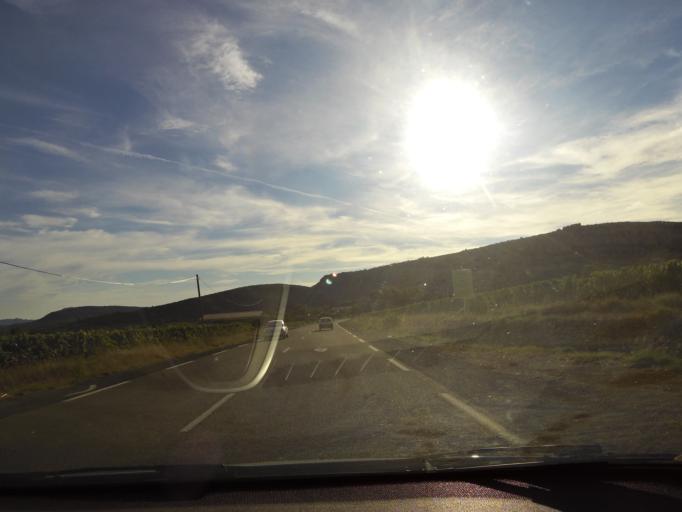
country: FR
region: Languedoc-Roussillon
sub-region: Departement de l'Herault
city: Claret
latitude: 43.8725
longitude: 3.9503
